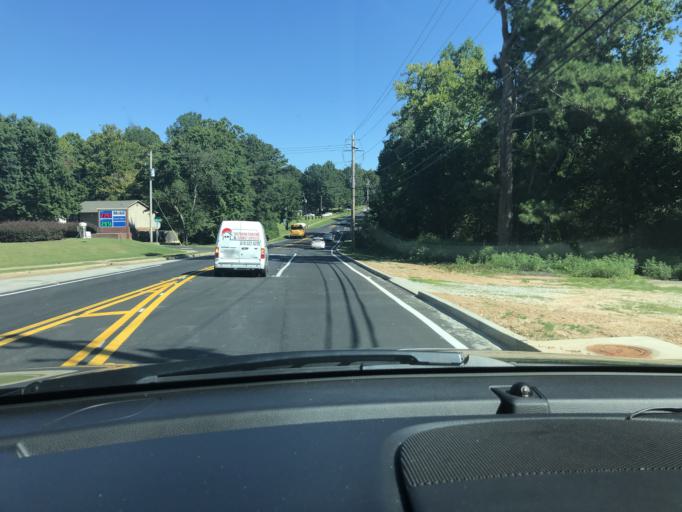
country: US
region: Georgia
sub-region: Gwinnett County
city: Lawrenceville
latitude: 33.9505
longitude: -83.9790
